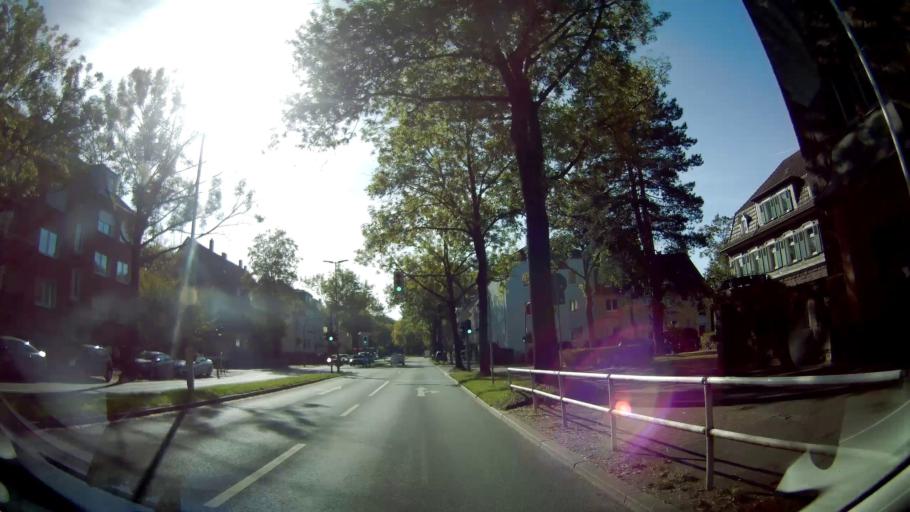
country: DE
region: North Rhine-Westphalia
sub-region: Regierungsbezirk Arnsberg
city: Bochum
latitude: 51.4694
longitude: 7.2177
